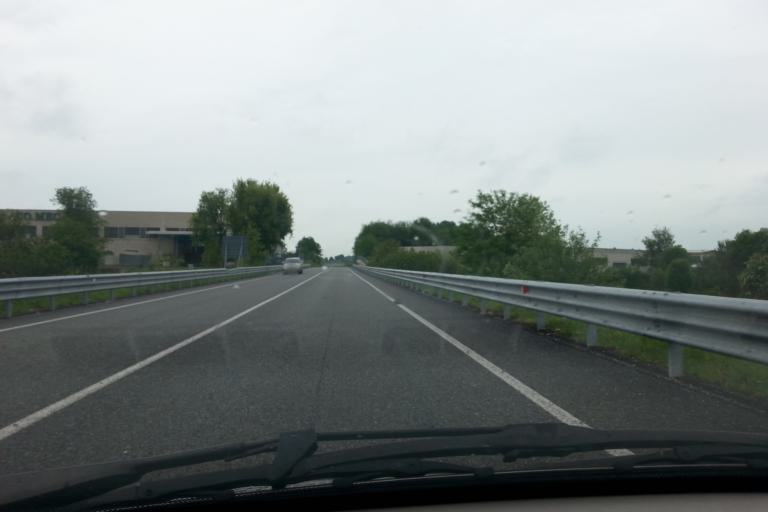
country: IT
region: Piedmont
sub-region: Provincia di Torino
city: Caselette
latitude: 45.1076
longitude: 7.5042
